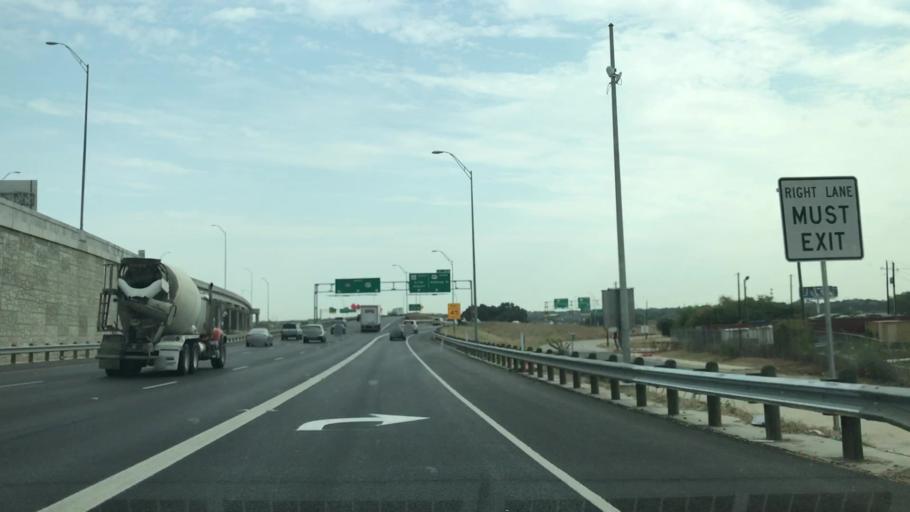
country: US
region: Texas
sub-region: Tarrant County
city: Fort Worth
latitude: 32.7622
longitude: -97.3177
